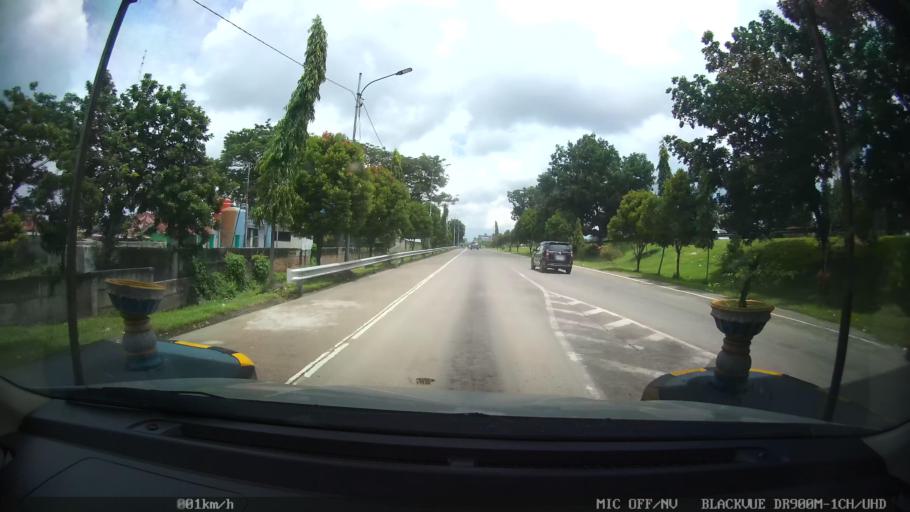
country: ID
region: North Sumatra
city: Medan
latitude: 3.5991
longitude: 98.7236
